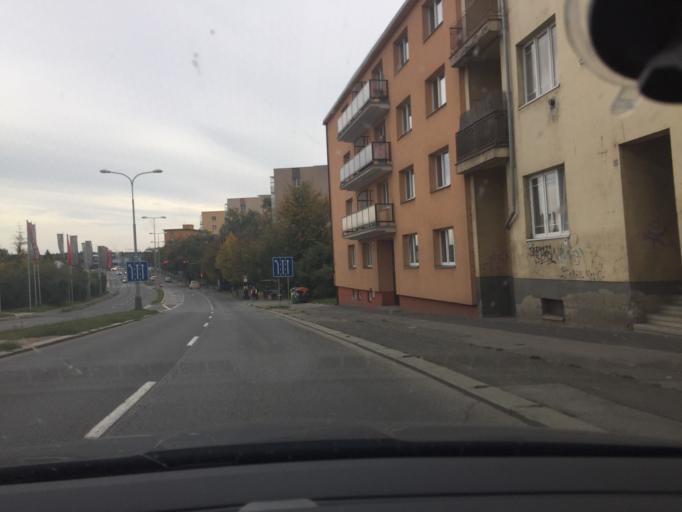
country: CZ
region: Praha
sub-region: Praha 9
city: Prosek
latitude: 50.0946
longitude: 14.4961
